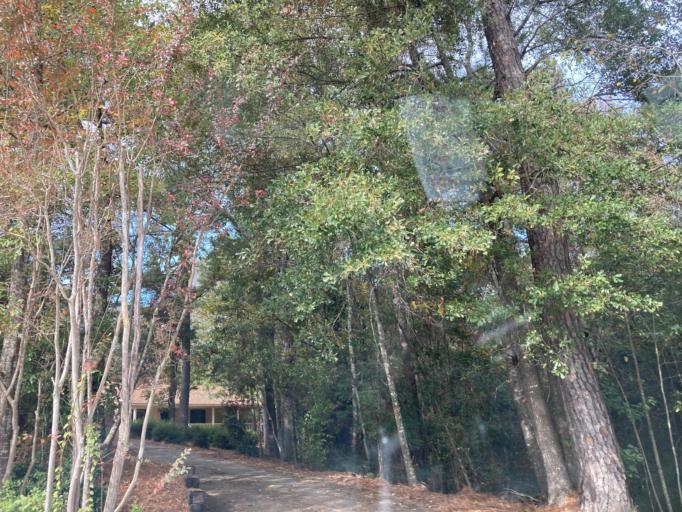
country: US
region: Mississippi
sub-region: Lamar County
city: West Hattiesburg
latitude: 31.3247
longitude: -89.4291
